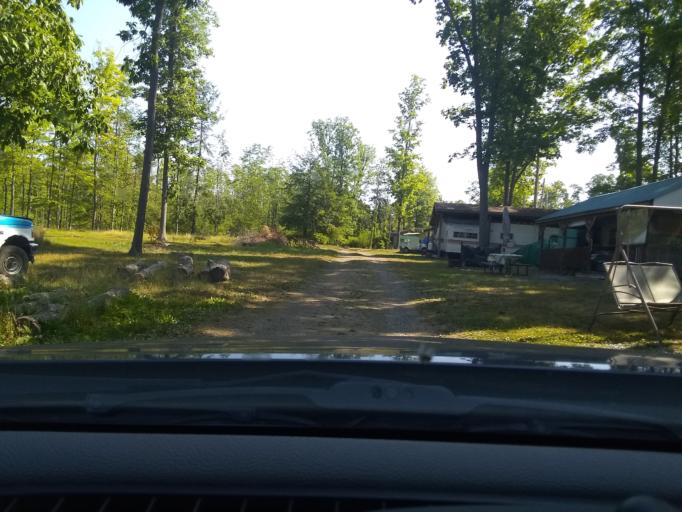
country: US
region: Pennsylvania
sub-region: Cambria County
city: Patton
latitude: 40.6552
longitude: -78.5122
